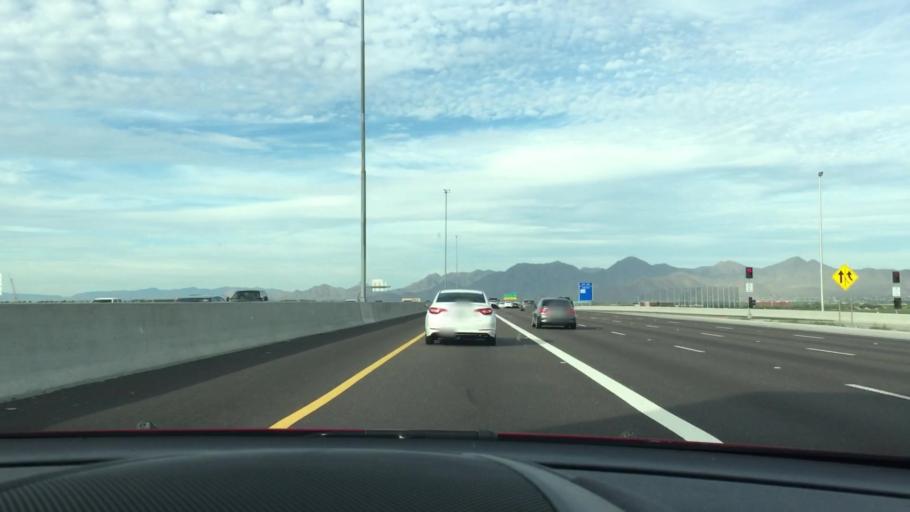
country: US
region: Arizona
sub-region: Maricopa County
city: Scottsdale
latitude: 33.5266
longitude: -111.8870
